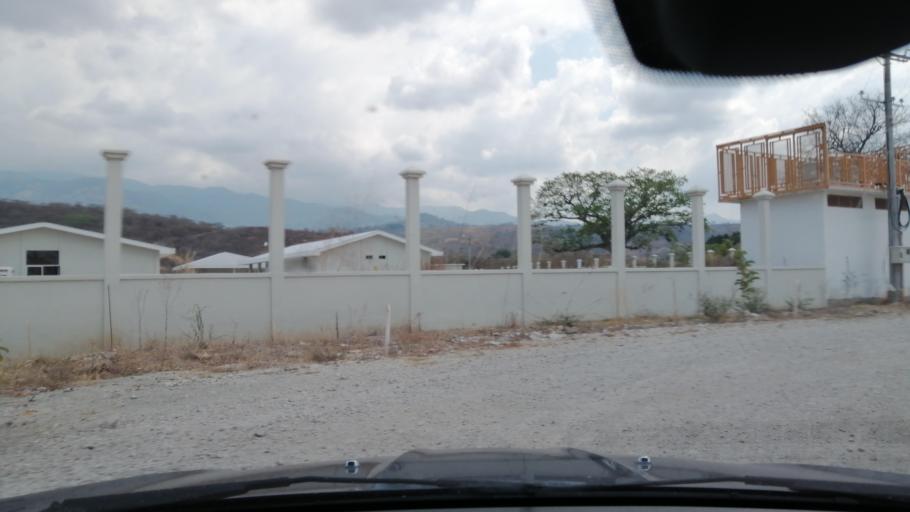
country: SV
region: Santa Ana
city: Metapan
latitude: 14.3392
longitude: -89.4482
